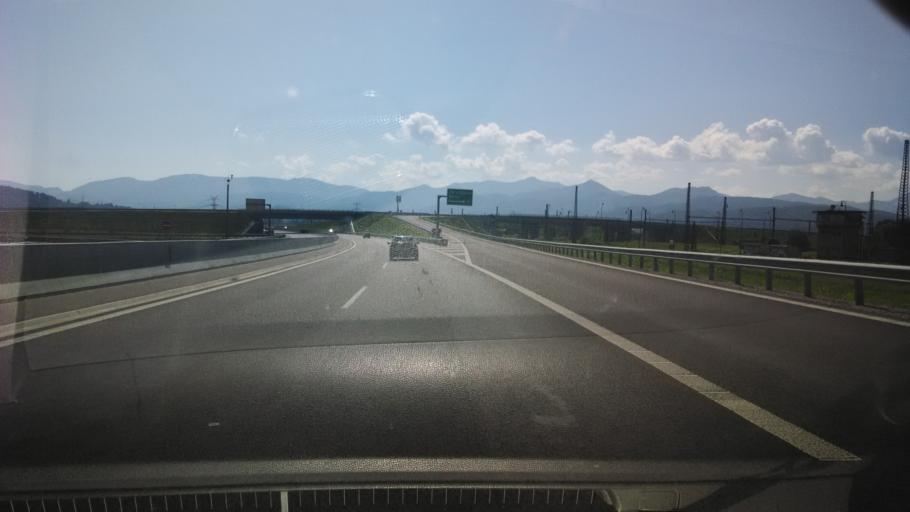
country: SK
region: Zilinsky
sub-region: Okres Zilina
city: Vrutky
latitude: 49.1094
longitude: 18.9529
